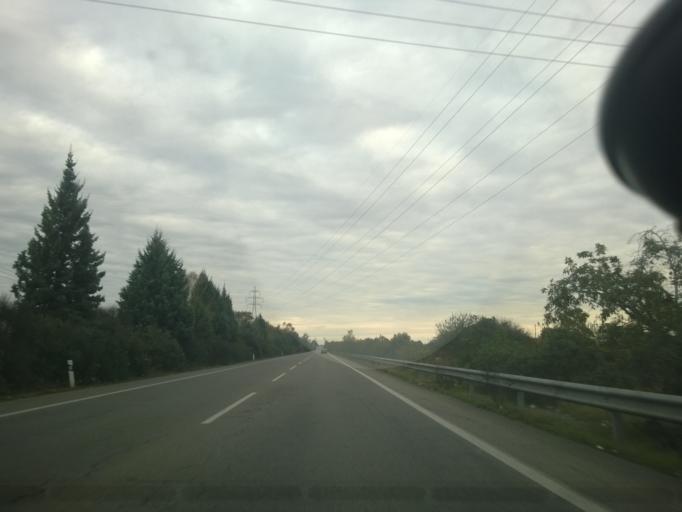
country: GR
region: Central Macedonia
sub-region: Nomos Pellis
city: Melissi
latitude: 40.7779
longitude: 22.3486
